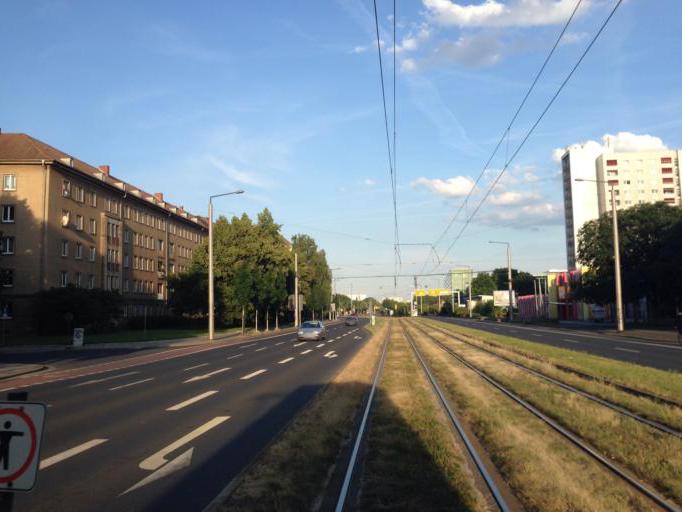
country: DE
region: Saxony
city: Dresden
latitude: 51.0473
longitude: 13.7511
